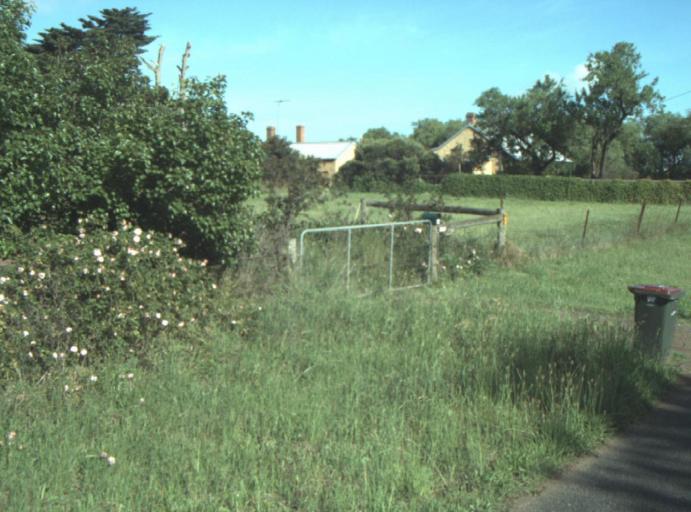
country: AU
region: Victoria
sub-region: Greater Geelong
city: Lara
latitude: -38.0138
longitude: 144.4019
